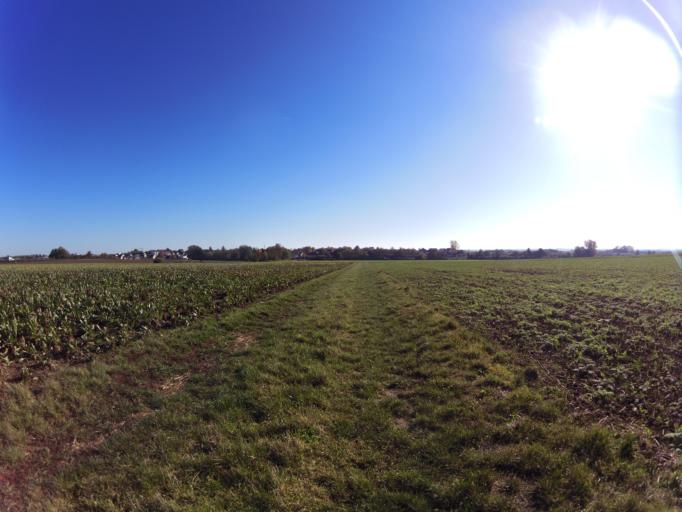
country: DE
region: Bavaria
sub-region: Regierungsbezirk Unterfranken
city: Giebelstadt
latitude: 49.6606
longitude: 9.9338
